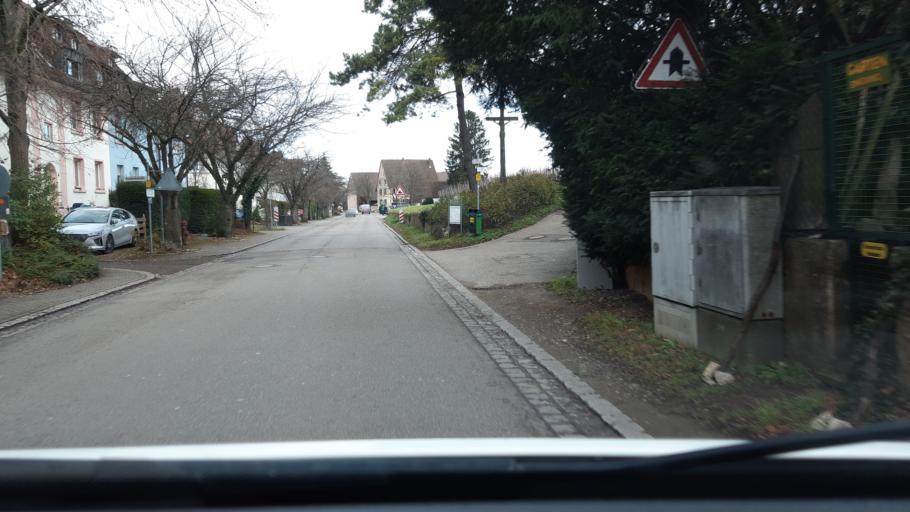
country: DE
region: Baden-Wuerttemberg
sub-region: Freiburg Region
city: Bad Krozingen
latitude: 47.8872
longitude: 7.7289
